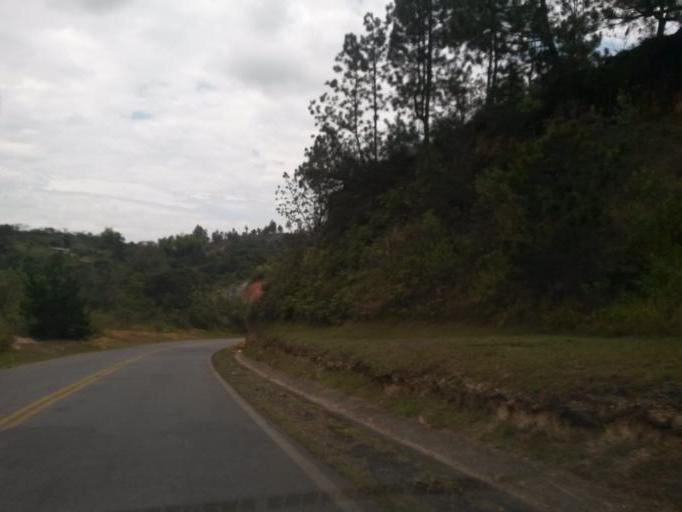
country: CO
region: Cauca
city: Lopez
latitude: 2.4657
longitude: -76.7355
